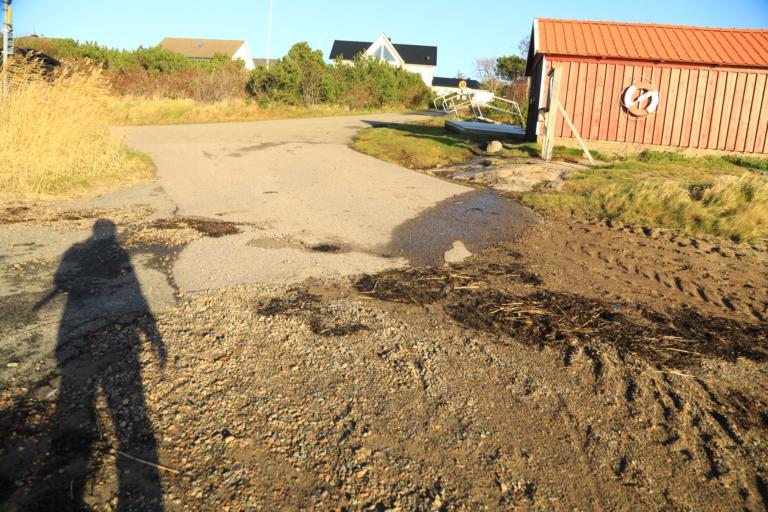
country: SE
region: Halland
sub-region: Varbergs Kommun
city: Varberg
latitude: 57.1686
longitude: 12.2108
